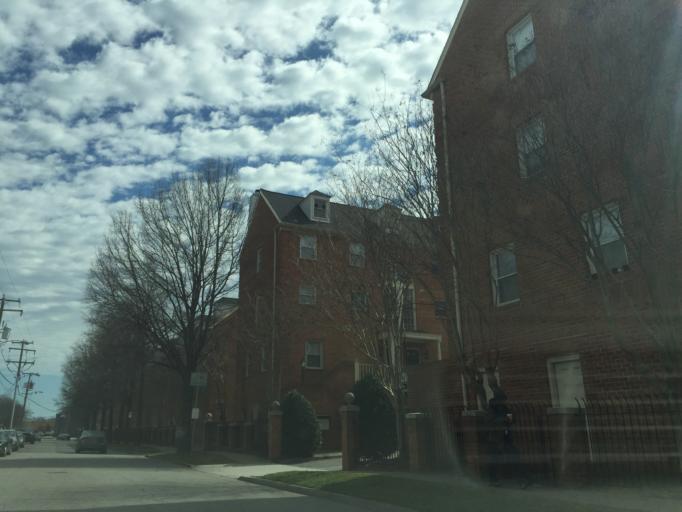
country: US
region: Virginia
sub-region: City of Norfolk
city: Norfolk
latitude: 36.8691
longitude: -76.2941
